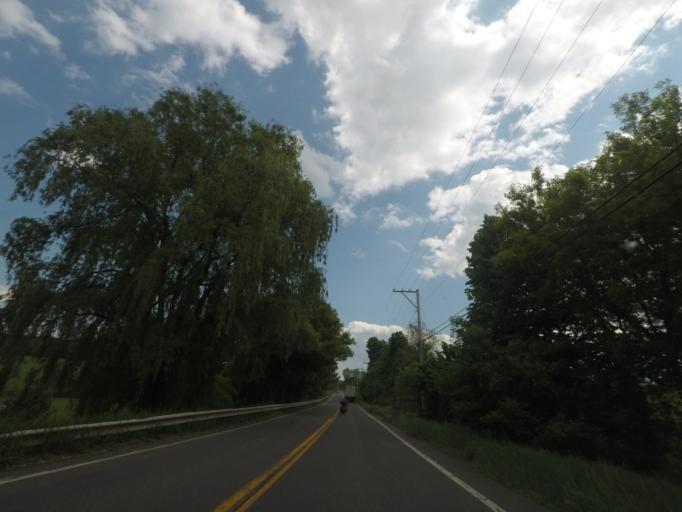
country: US
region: New York
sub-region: Dutchess County
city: Pine Plains
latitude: 42.0407
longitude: -73.6167
